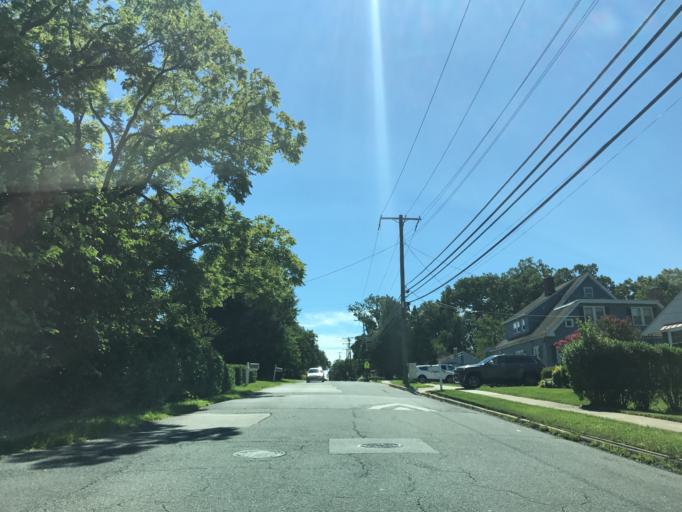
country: US
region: Maryland
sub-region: Howard County
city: Ilchester
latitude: 39.2795
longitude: -76.7714
